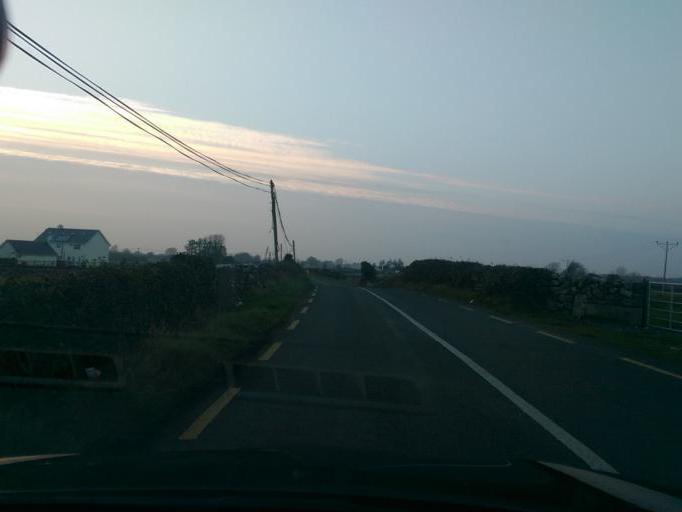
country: IE
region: Connaught
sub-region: County Galway
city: Loughrea
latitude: 53.2176
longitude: -8.6178
